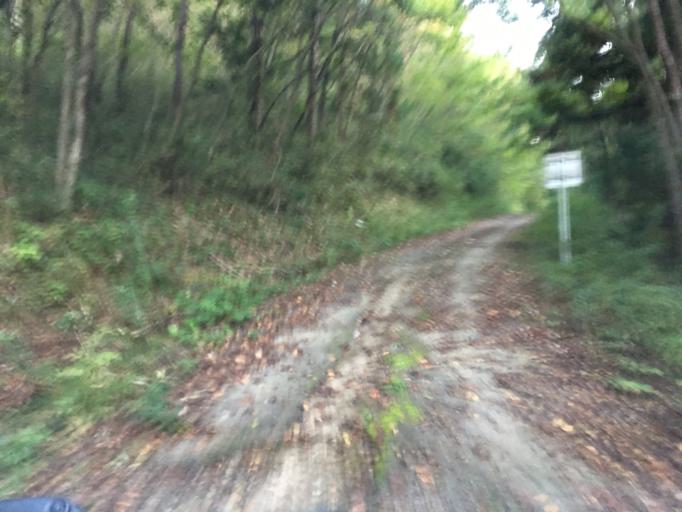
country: JP
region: Fukushima
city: Yanagawamachi-saiwaicho
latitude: 37.8414
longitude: 140.6268
